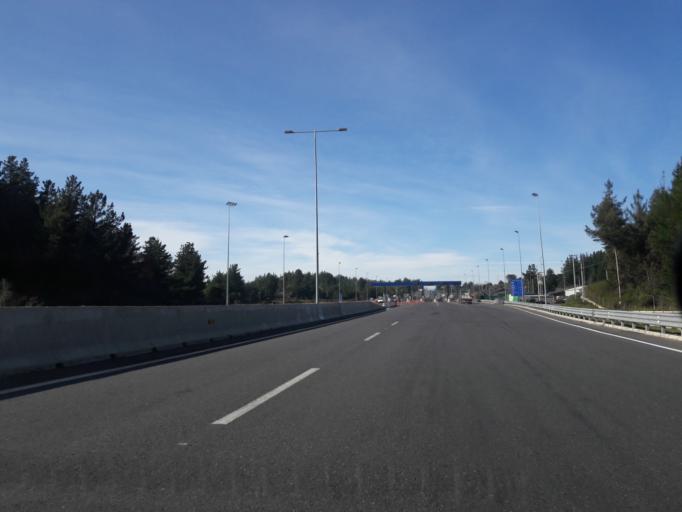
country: CL
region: Biobio
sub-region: Provincia de Biobio
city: Yumbel
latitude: -36.9600
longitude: -72.7311
